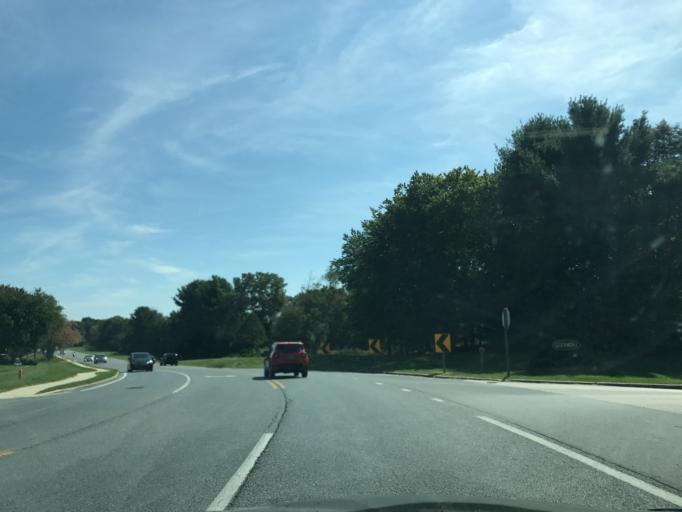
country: US
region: Maryland
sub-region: Howard County
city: Columbia
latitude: 39.2283
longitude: -76.8269
